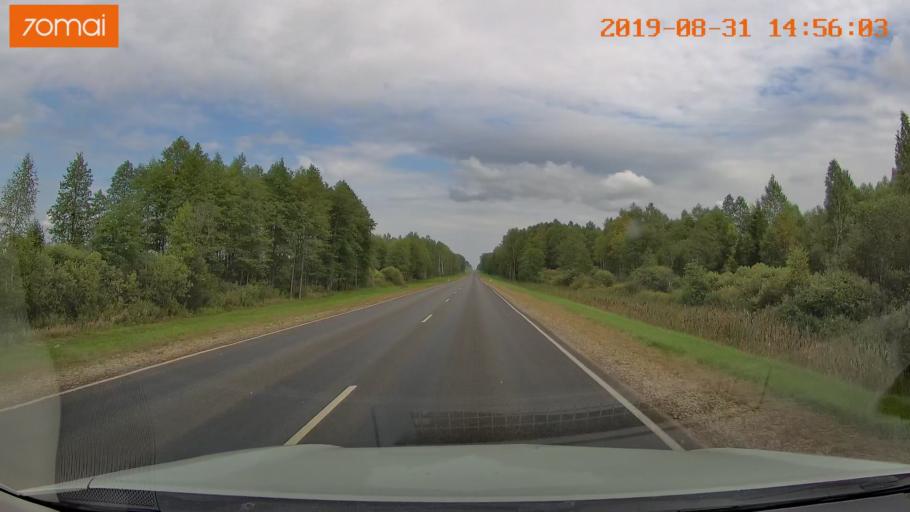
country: RU
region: Kaluga
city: Spas-Demensk
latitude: 54.3022
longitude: 33.9290
